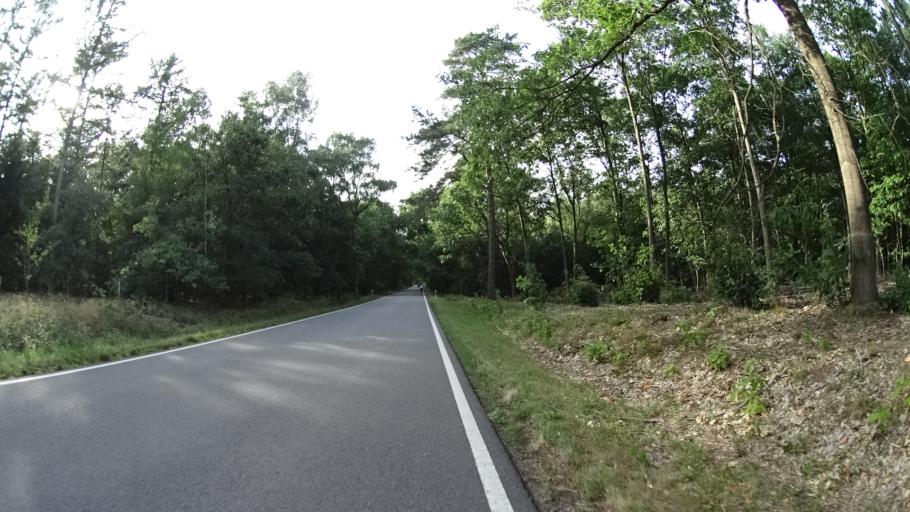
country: DE
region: Lower Saxony
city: Undeloh
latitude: 53.1723
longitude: 9.8910
